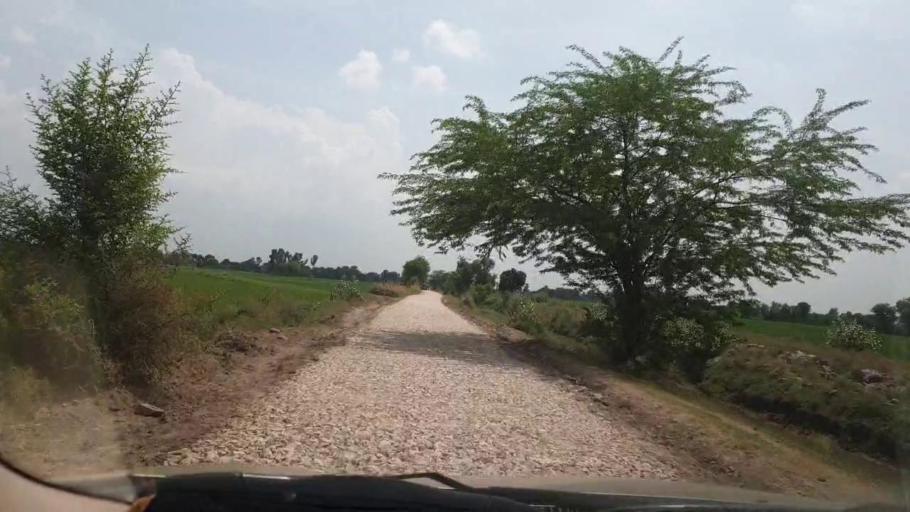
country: PK
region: Sindh
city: Larkana
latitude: 27.5676
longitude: 68.1102
